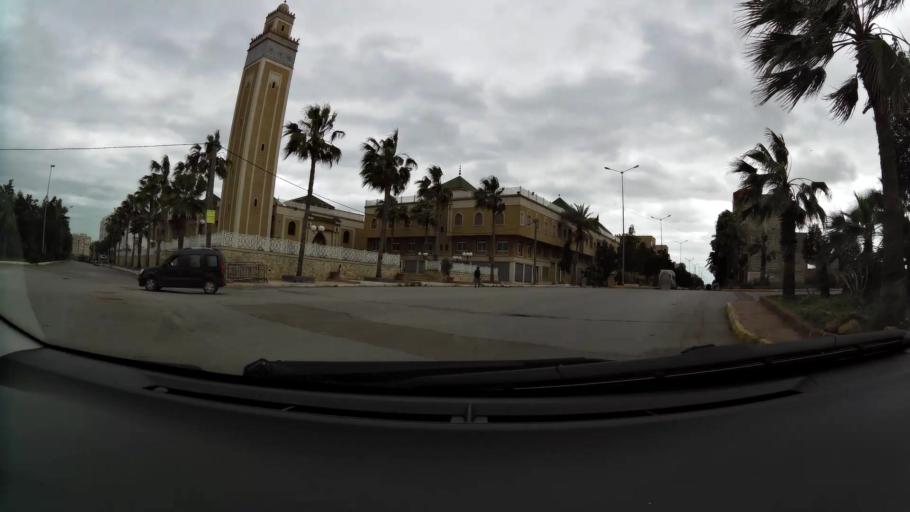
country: MA
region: Grand Casablanca
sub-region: Mediouna
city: Tit Mellil
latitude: 33.5558
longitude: -7.5358
